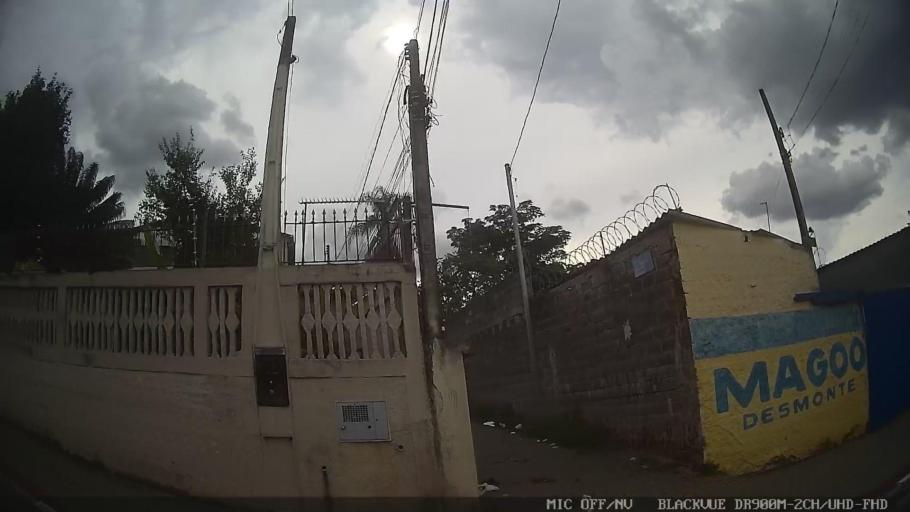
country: BR
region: Sao Paulo
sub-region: Poa
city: Poa
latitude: -23.5369
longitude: -46.3458
